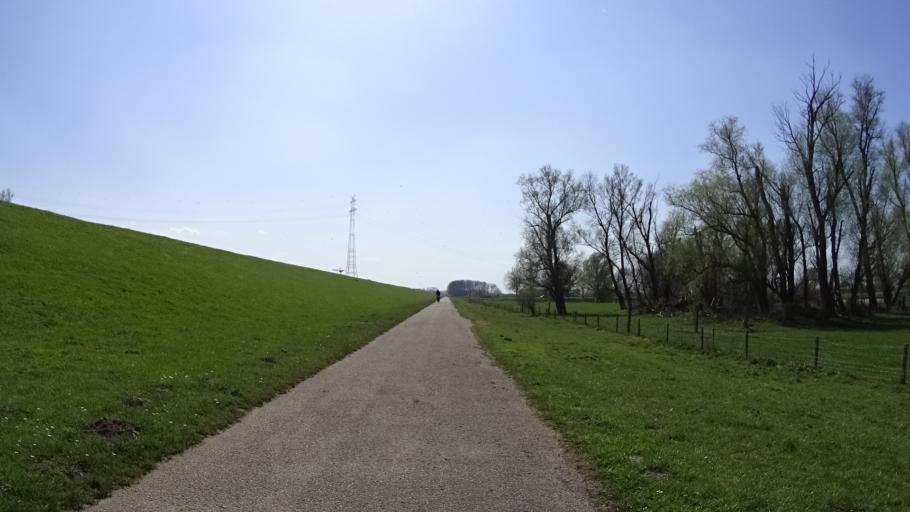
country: DE
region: Lower Saxony
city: Weener
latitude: 53.1533
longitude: 7.3713
